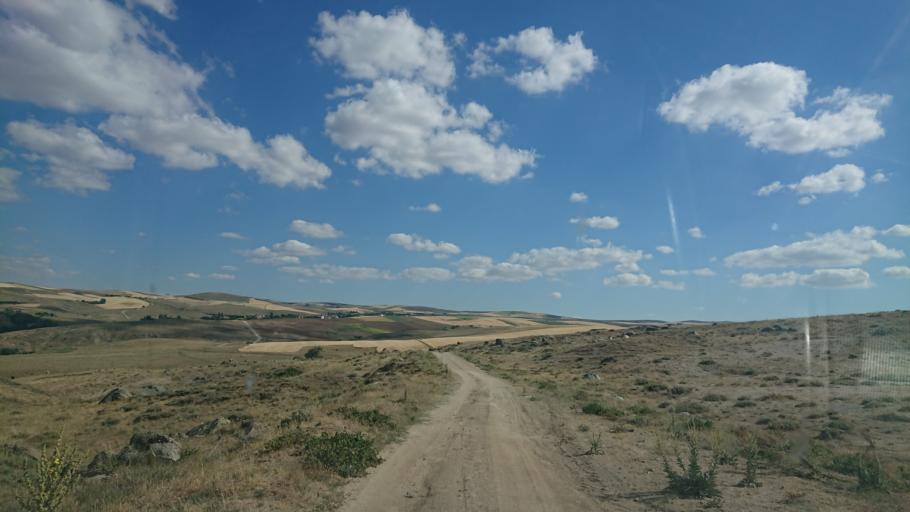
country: TR
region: Aksaray
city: Sariyahsi
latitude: 38.9240
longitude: 33.8524
